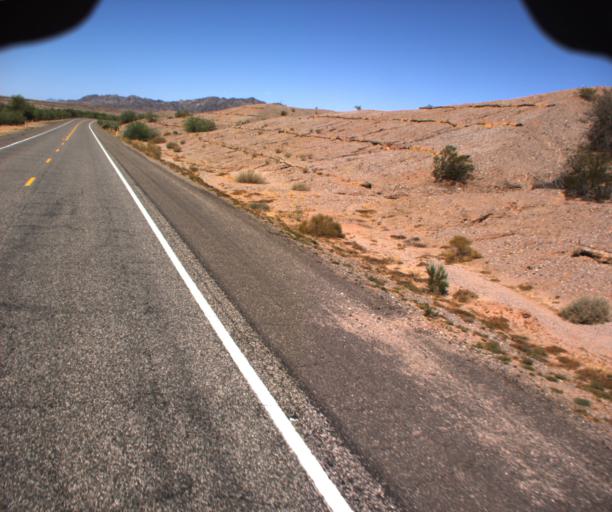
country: US
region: Arizona
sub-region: La Paz County
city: Parker
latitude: 33.9939
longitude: -114.2029
